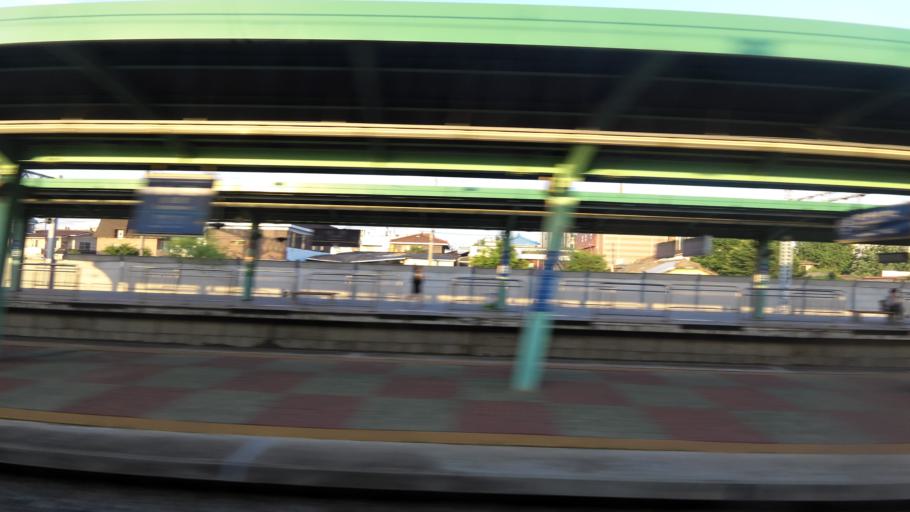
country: KR
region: Chungcheongnam-do
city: Seonghwan
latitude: 36.9168
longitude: 127.1269
